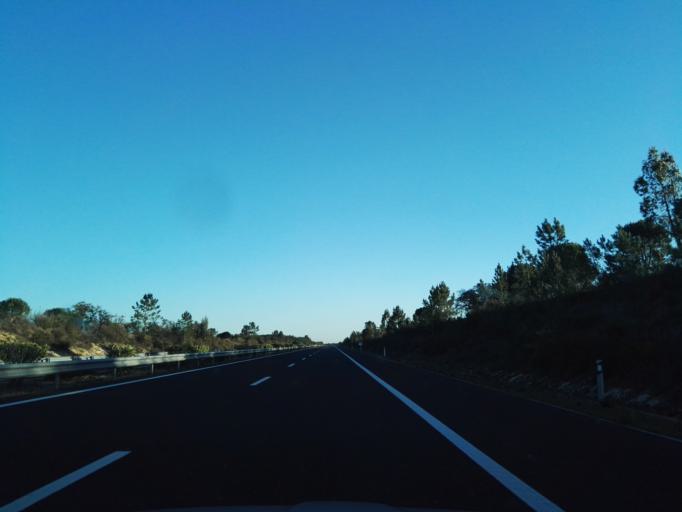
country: PT
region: Santarem
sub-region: Benavente
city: Poceirao
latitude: 38.8088
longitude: -8.7042
